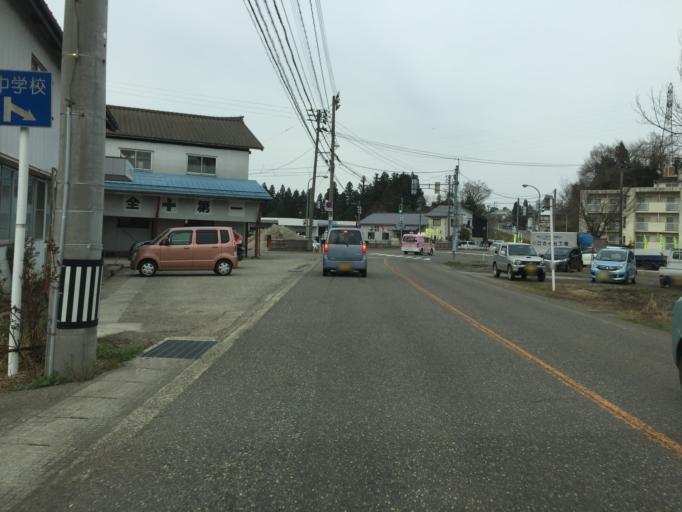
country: JP
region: Niigata
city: Tochio-honcho
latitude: 37.4849
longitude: 139.0072
